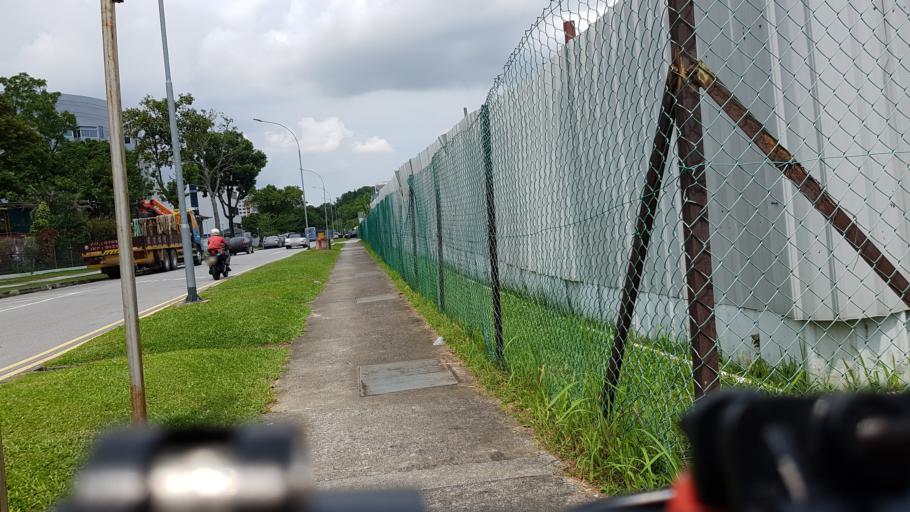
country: MY
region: Johor
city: Kampung Pasir Gudang Baru
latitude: 1.4424
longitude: 103.8334
